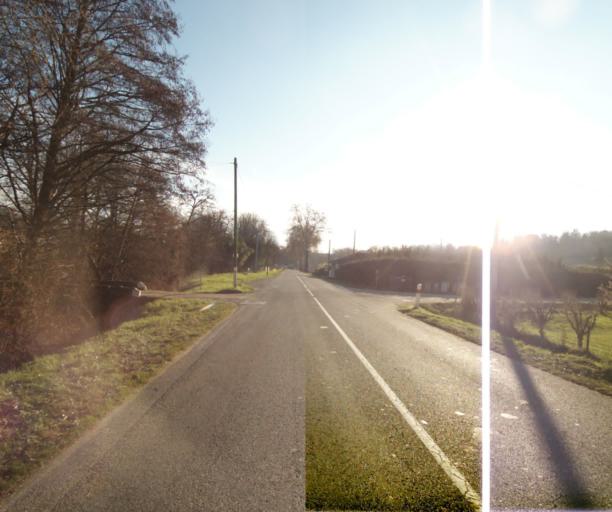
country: FR
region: Midi-Pyrenees
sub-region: Departement du Tarn-et-Garonne
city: Moissac
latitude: 44.1244
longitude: 1.1033
